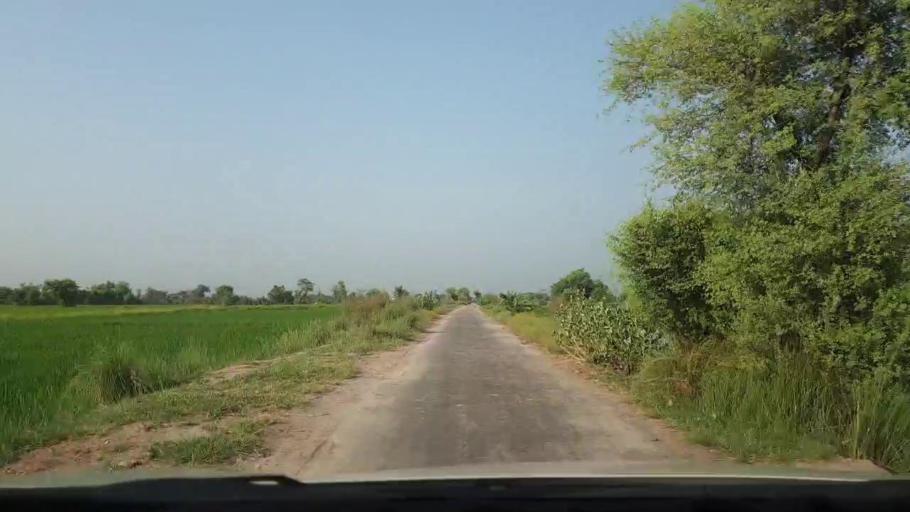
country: PK
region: Sindh
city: Larkana
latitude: 27.4955
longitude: 68.1707
